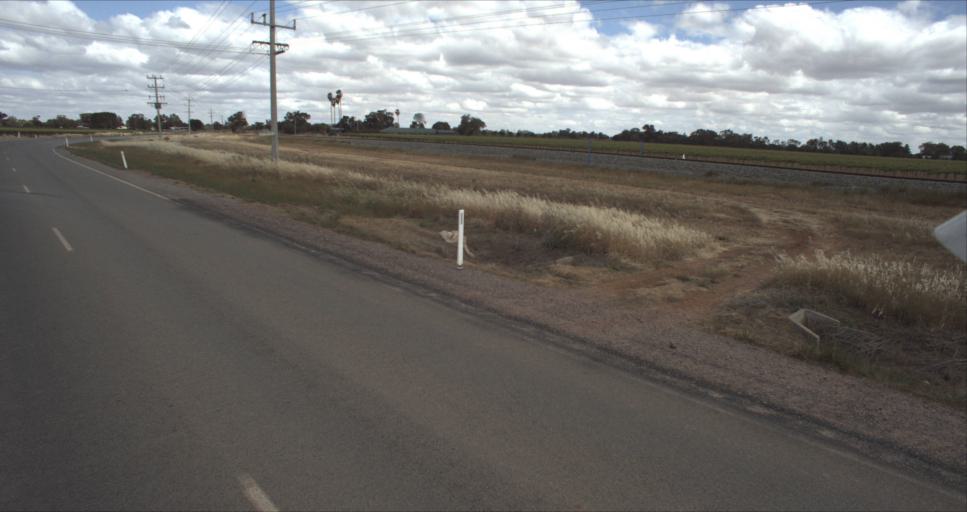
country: AU
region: New South Wales
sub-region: Leeton
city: Leeton
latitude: -34.5853
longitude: 146.4033
